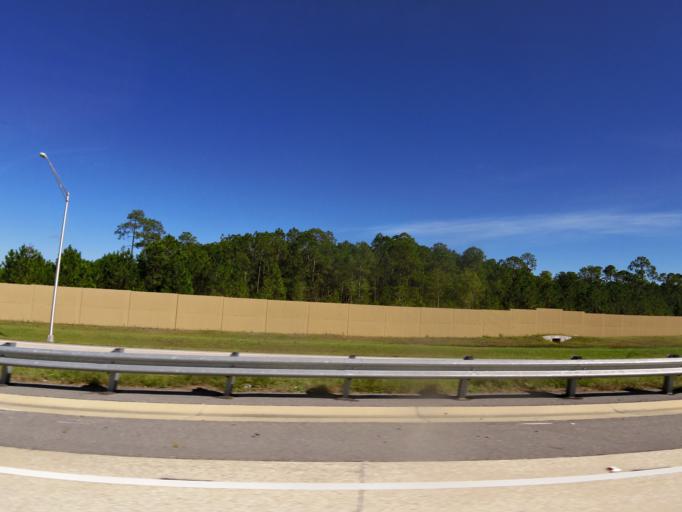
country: US
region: Florida
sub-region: Saint Johns County
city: Fruit Cove
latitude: 30.1164
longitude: -81.5128
